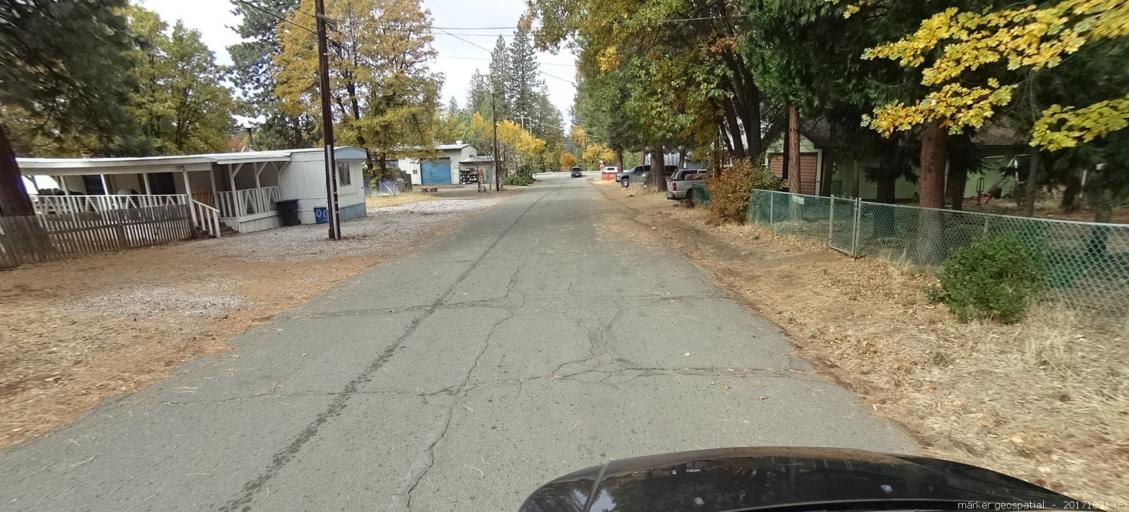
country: US
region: California
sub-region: Shasta County
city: Burney
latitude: 40.9166
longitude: -121.6265
